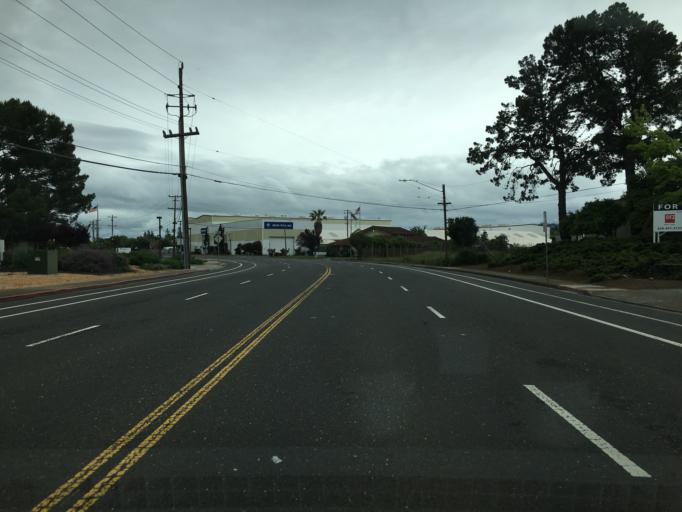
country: US
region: California
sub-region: San Mateo County
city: San Carlos
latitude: 37.5174
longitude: -122.2637
